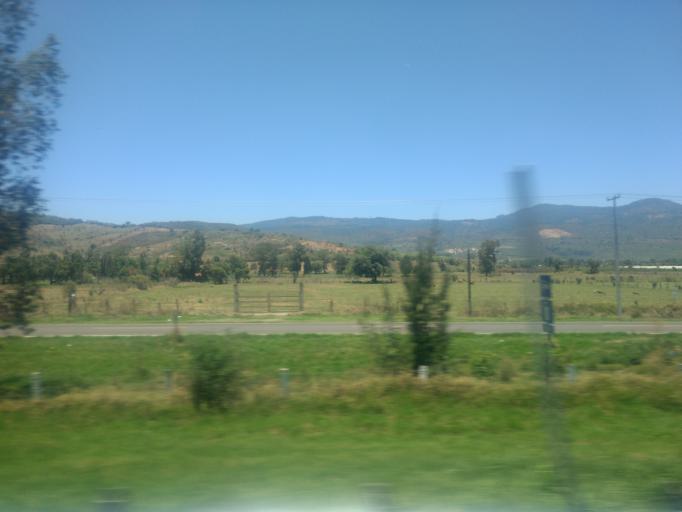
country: MX
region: Jalisco
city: San Andres Ixtlan
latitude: 19.8245
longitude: -103.4946
